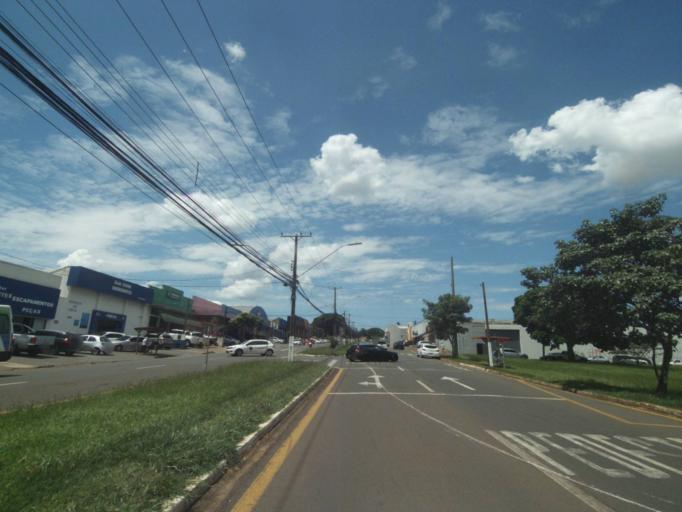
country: BR
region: Parana
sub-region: Londrina
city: Londrina
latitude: -23.3016
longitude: -51.1948
